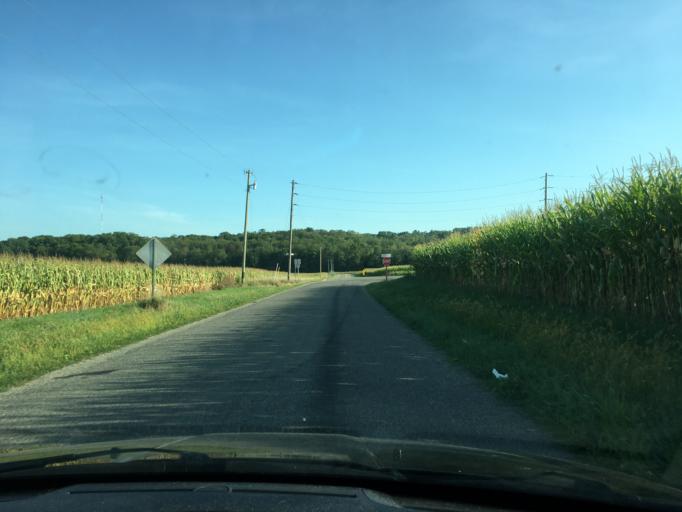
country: US
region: Ohio
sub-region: Champaign County
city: North Lewisburg
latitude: 40.2130
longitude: -83.6571
